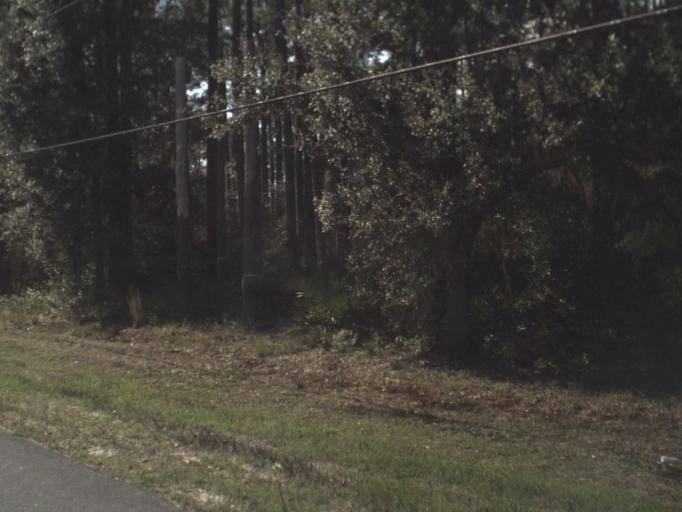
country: US
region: Florida
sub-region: Wakulla County
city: Crawfordville
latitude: 30.0815
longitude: -84.3927
